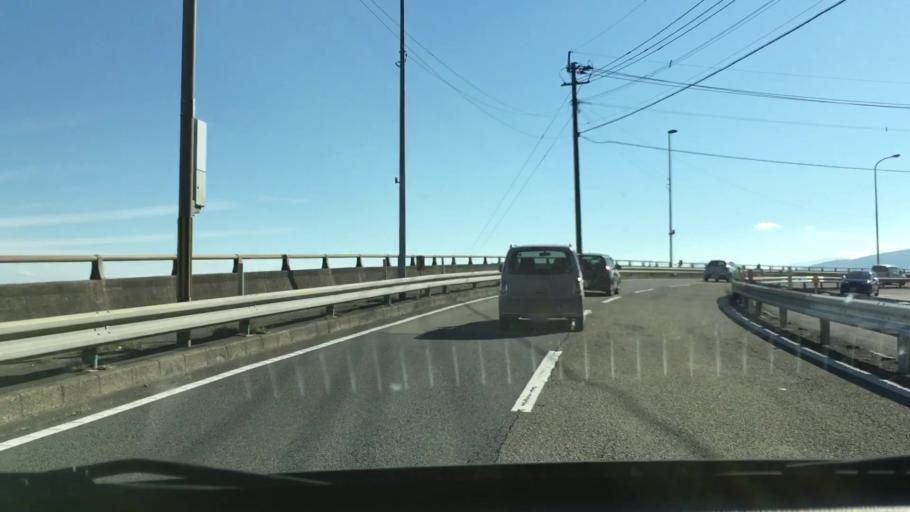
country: JP
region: Kagoshima
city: Kajiki
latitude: 31.6591
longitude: 130.6188
